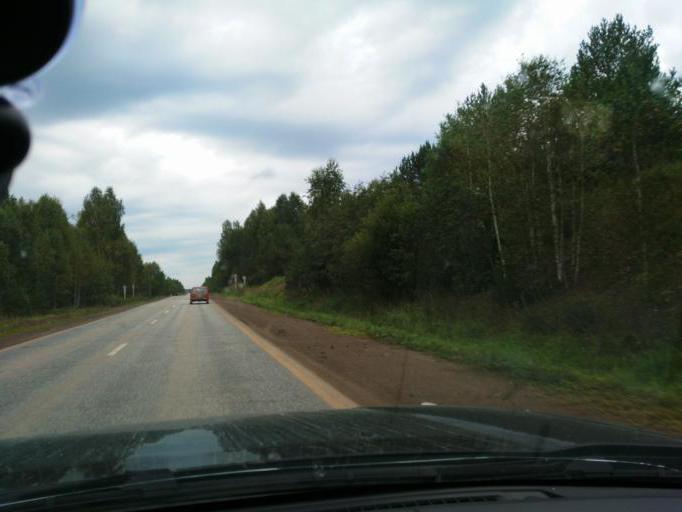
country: RU
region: Perm
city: Chernushka
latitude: 56.7954
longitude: 56.0782
